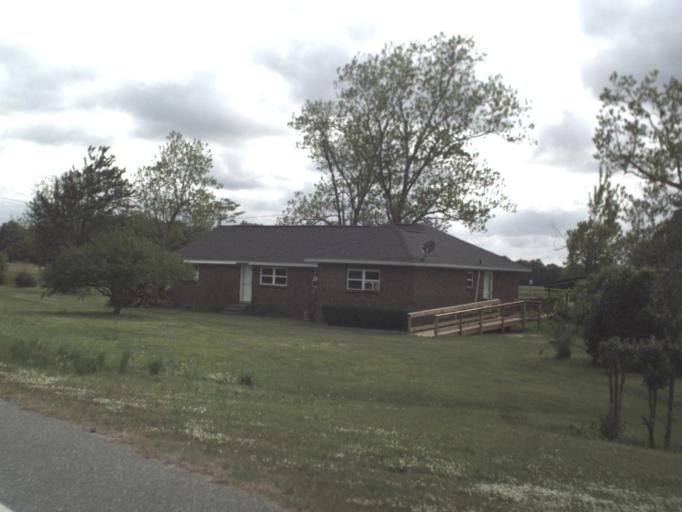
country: US
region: Florida
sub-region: Santa Rosa County
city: Point Baker
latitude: 30.8827
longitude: -87.0521
